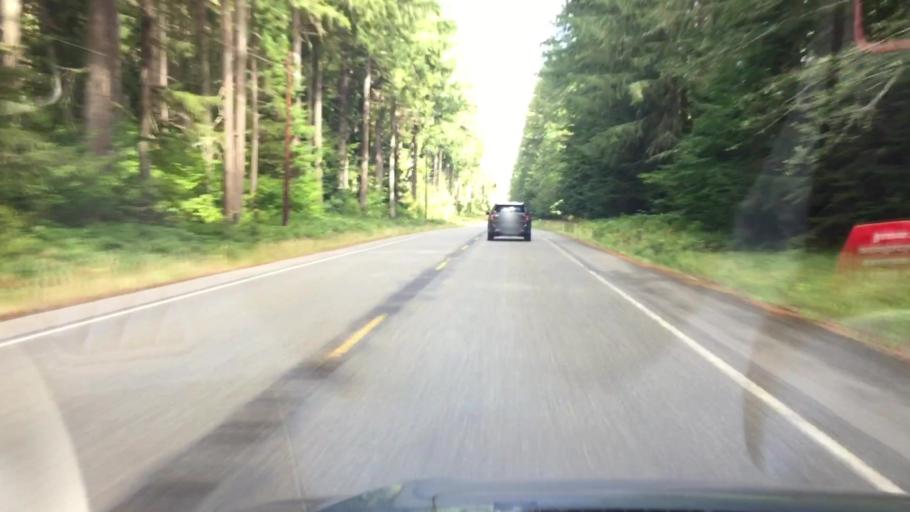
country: US
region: Washington
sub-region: Pierce County
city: Eatonville
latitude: 46.7561
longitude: -122.0847
